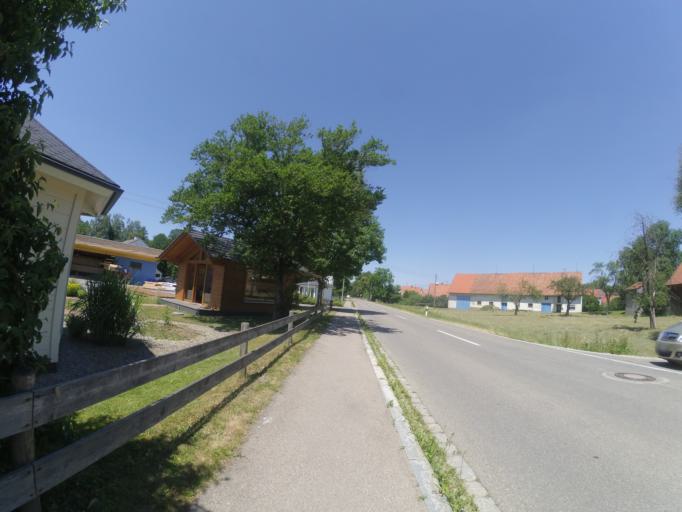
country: DE
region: Bavaria
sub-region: Swabia
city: Ottobeuren
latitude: 47.9293
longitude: 10.3064
